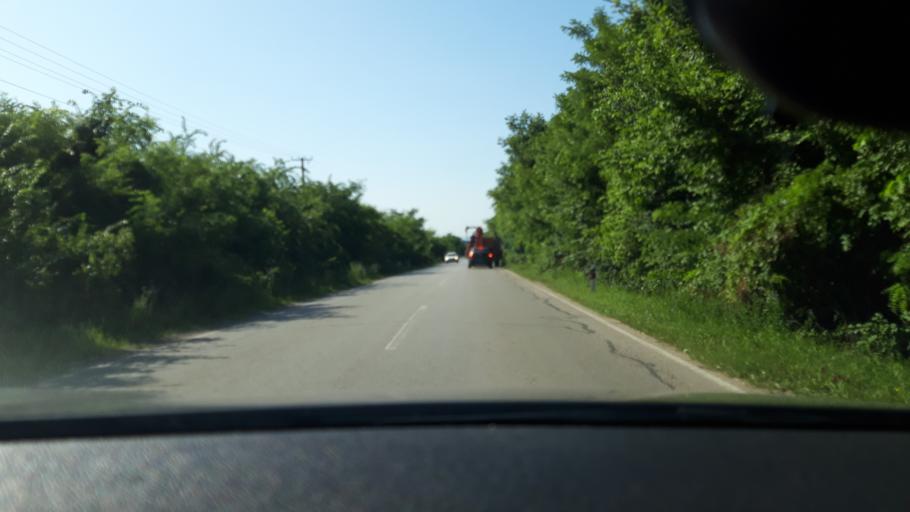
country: RS
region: Central Serbia
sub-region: Nisavski Okrug
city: Nis
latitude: 43.3899
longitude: 21.8153
